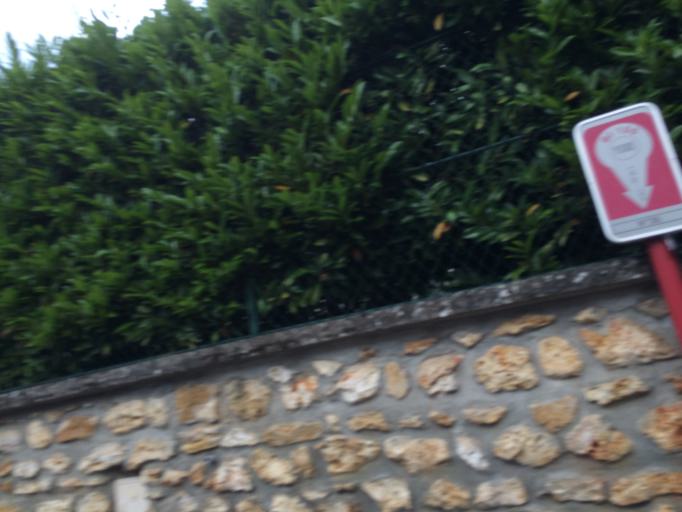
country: FR
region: Ile-de-France
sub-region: Departement de l'Essonne
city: Verrieres-le-Buisson
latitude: 48.7499
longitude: 2.2670
